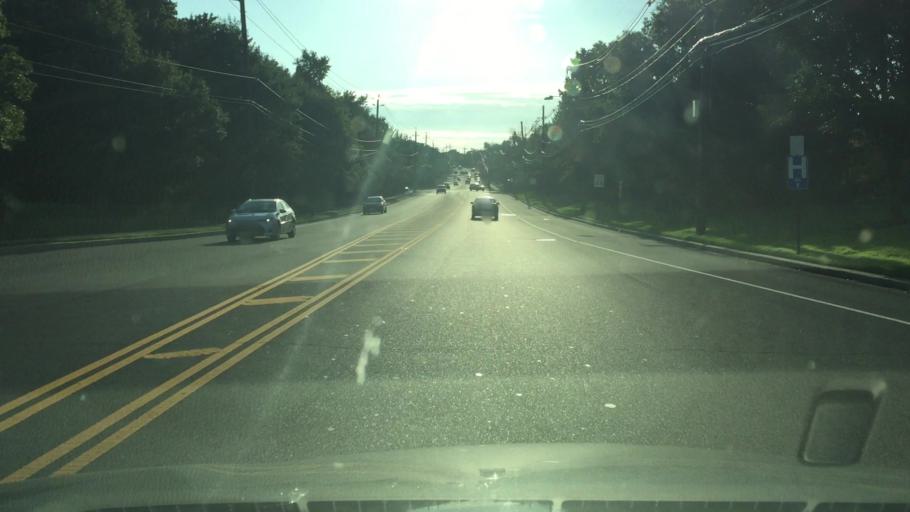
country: US
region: New Jersey
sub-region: Middlesex County
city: Edison
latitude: 40.5422
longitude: -74.3967
